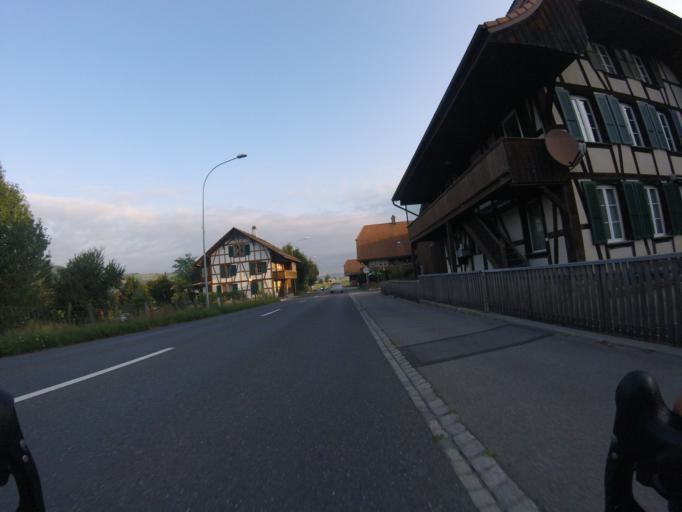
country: CH
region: Bern
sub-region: Bern-Mittelland District
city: Niederwichtrach
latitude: 46.8513
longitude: 7.5748
